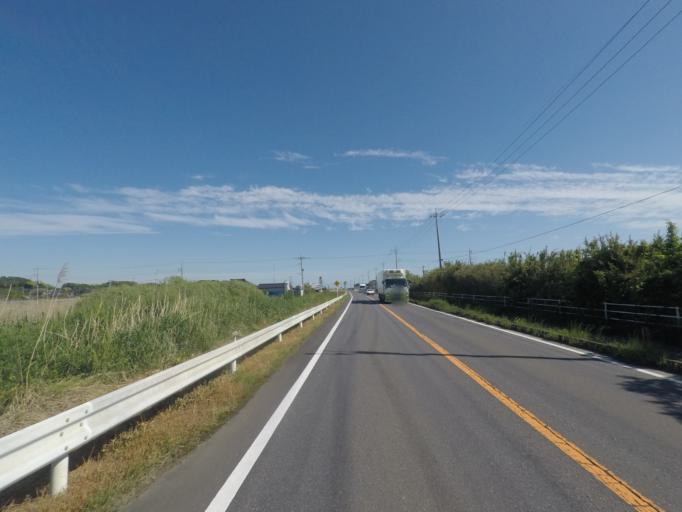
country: JP
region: Ibaraki
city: Inashiki
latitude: 36.0734
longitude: 140.4228
